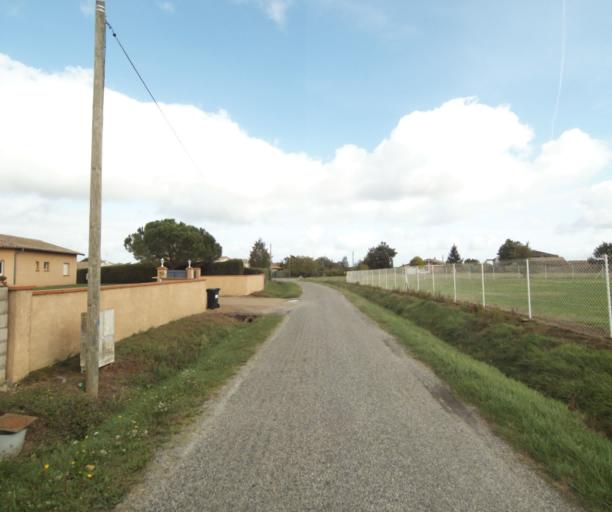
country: FR
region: Midi-Pyrenees
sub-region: Departement du Tarn-et-Garonne
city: Finhan
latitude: 43.8967
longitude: 1.1310
